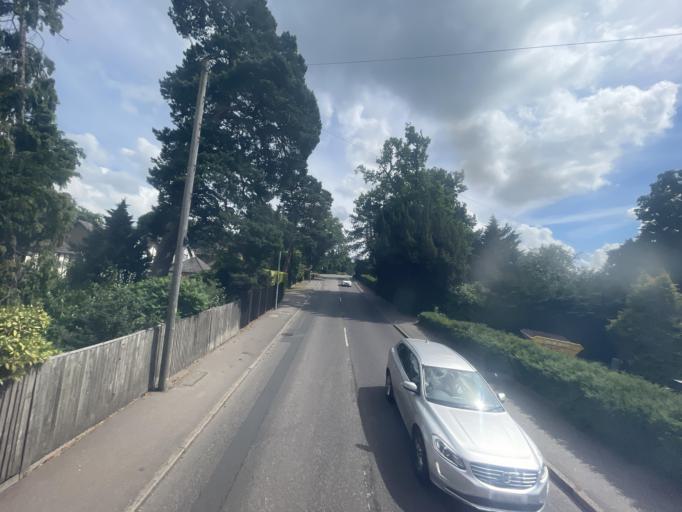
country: GB
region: England
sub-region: Kent
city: Biggin Hill
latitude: 51.3590
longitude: 0.0310
